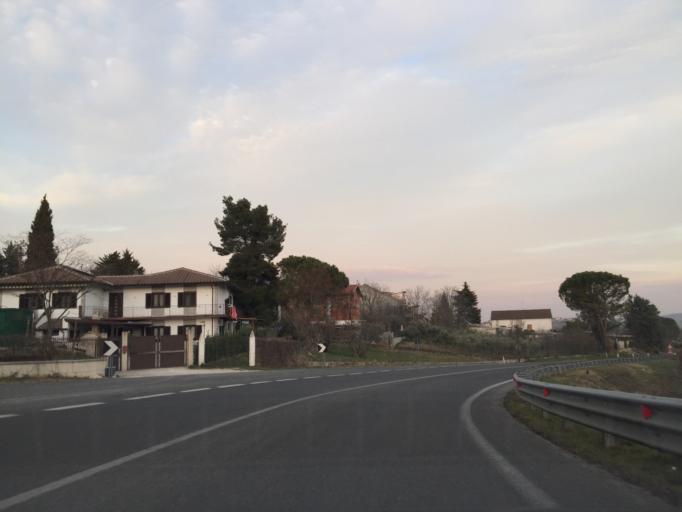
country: IT
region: Molise
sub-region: Provincia di Campobasso
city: Campobasso
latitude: 41.5617
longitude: 14.6938
